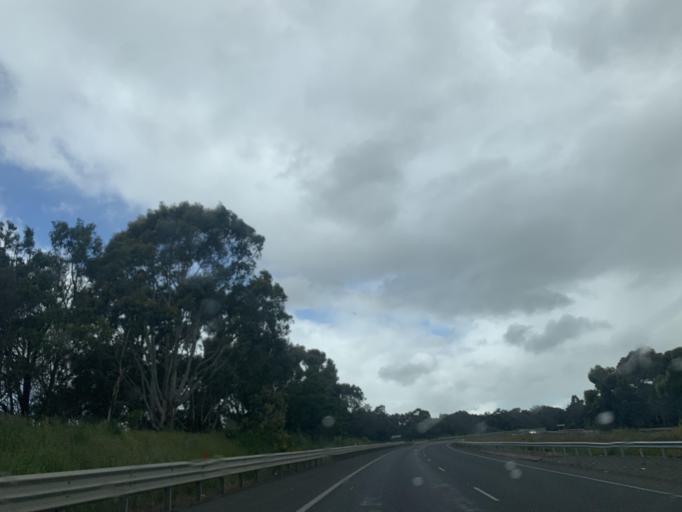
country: AU
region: Victoria
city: Brown Hill
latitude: -37.5490
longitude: 143.9056
